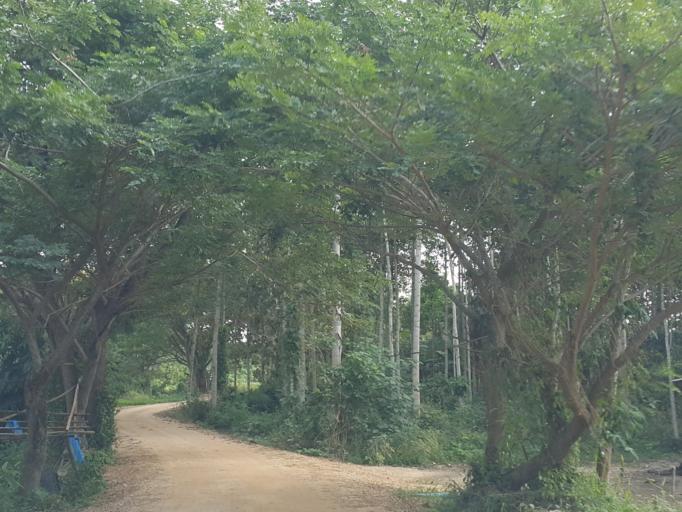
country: TH
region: Lampang
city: Hang Chat
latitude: 18.4804
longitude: 99.4041
